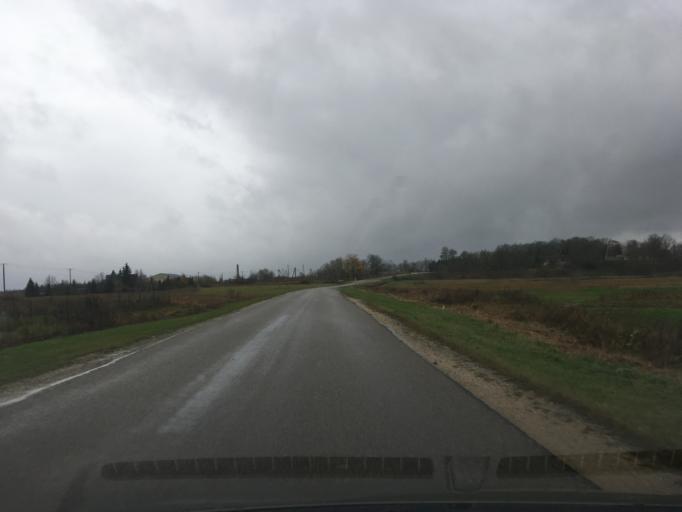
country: EE
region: Laeaene
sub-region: Lihula vald
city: Lihula
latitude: 58.6954
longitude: 23.8494
